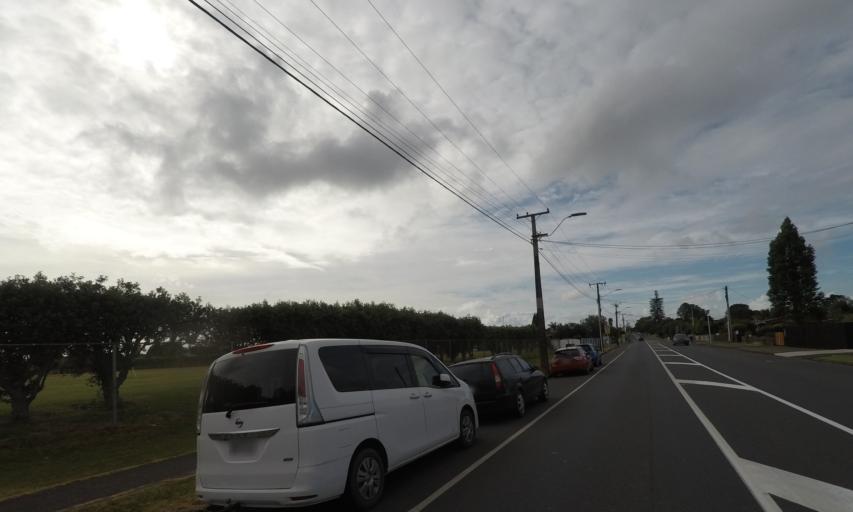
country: NZ
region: Northland
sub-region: Whangarei
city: Whangarei
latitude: -35.6860
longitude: 174.3024
